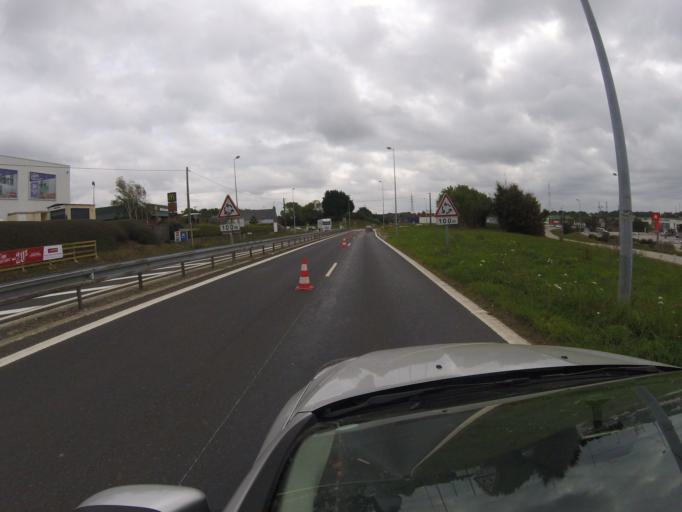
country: FR
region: Lower Normandy
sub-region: Departement de la Manche
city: La Glacerie
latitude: 49.6008
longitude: -1.5978
